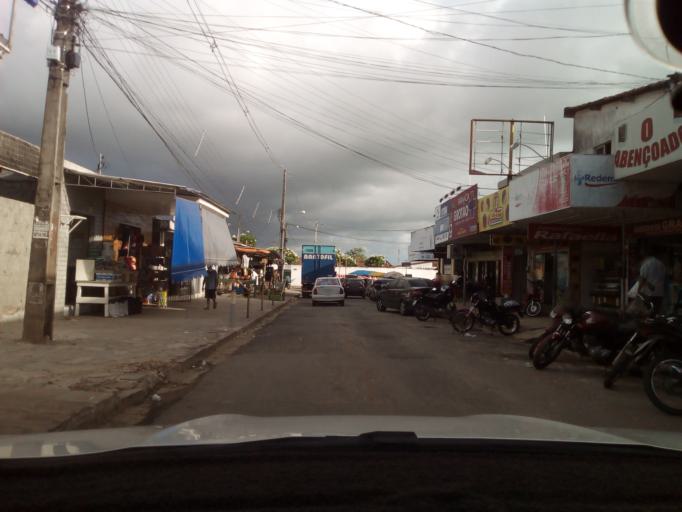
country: BR
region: Paraiba
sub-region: Joao Pessoa
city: Joao Pessoa
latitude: -7.1860
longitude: -34.8829
